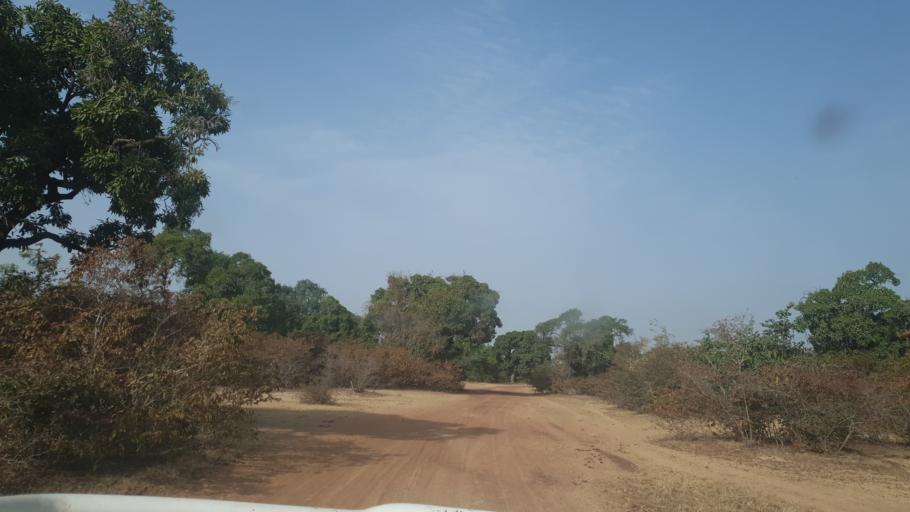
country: ML
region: Segou
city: Baroueli
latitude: 13.3625
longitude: -6.9207
